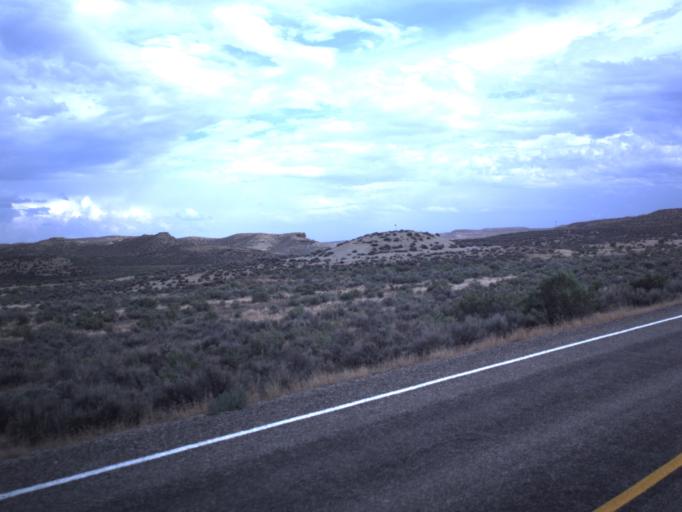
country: US
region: Colorado
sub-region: Rio Blanco County
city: Rangely
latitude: 40.0436
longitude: -109.1862
